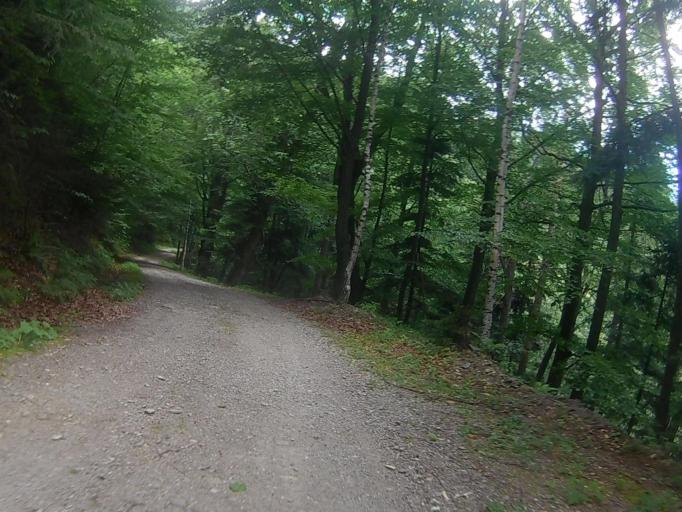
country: SI
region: Selnica ob Dravi
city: Selnica ob Dravi
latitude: 46.5222
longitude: 15.4805
